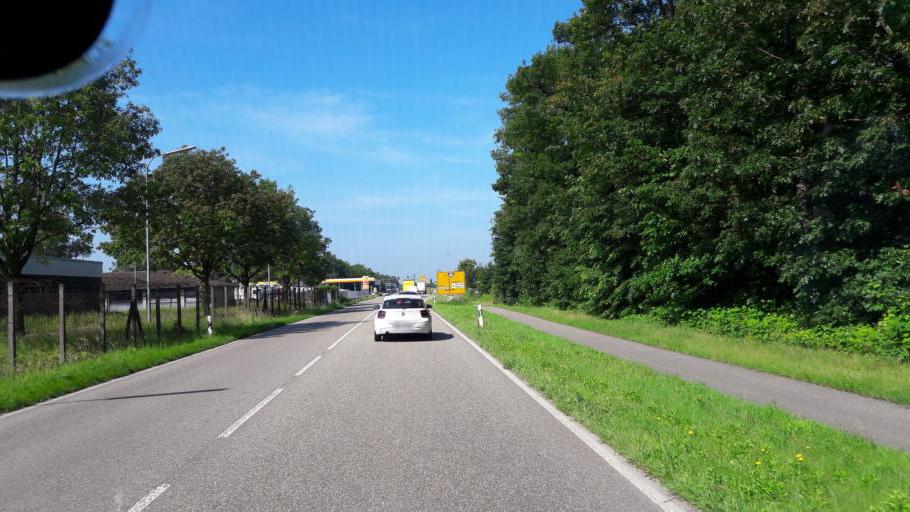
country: DE
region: Baden-Wuerttemberg
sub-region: Karlsruhe Region
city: Muggensturm
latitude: 48.8862
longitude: 8.2719
